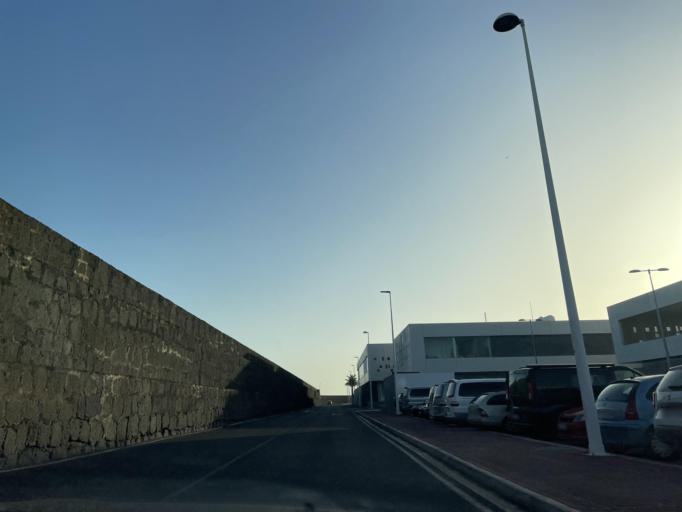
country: ES
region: Canary Islands
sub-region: Provincia de Las Palmas
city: Arrecife
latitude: 28.9618
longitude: -13.5387
